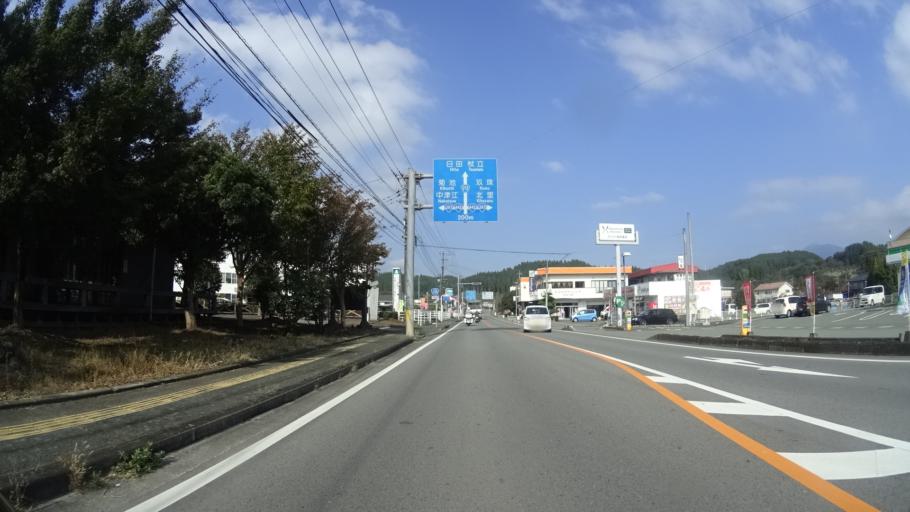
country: JP
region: Oita
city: Tsukawaki
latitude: 33.1221
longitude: 131.0614
